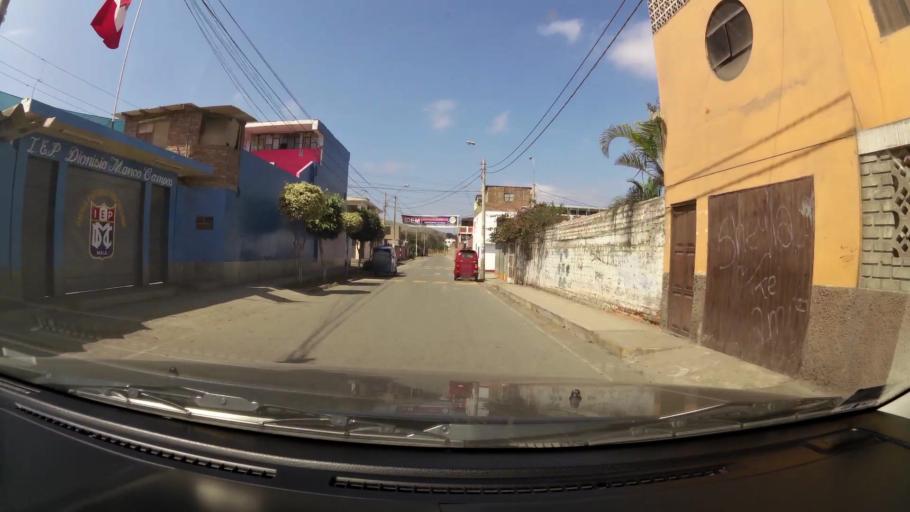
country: PE
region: Lima
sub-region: Provincia de Canete
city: Mala
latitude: -12.6598
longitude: -76.6293
